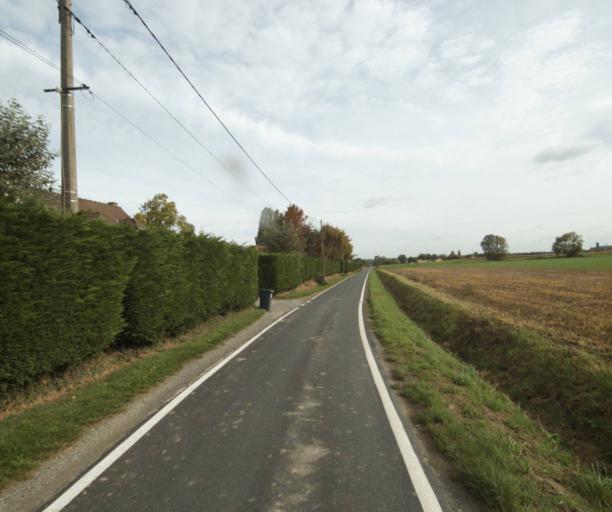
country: FR
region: Nord-Pas-de-Calais
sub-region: Departement du Nord
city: Radinghem-en-Weppes
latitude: 50.6193
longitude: 2.8901
